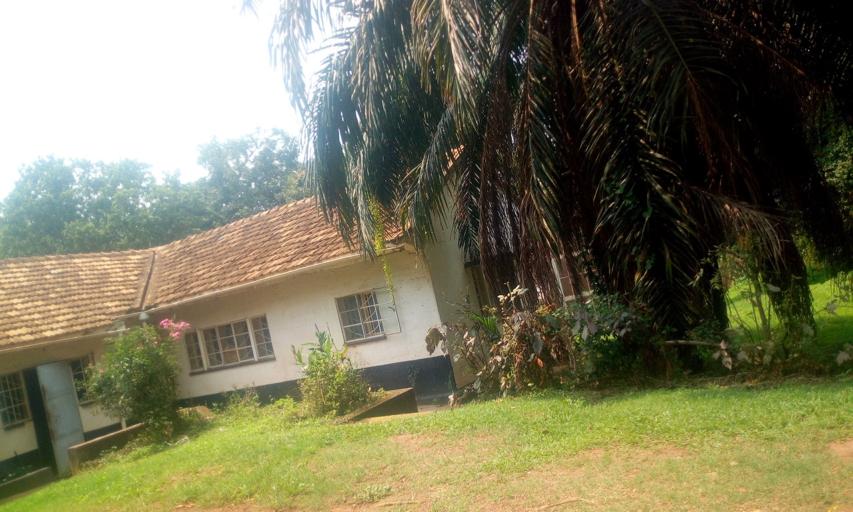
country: UG
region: Central Region
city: Kampala Central Division
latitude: 0.3324
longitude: 32.5712
